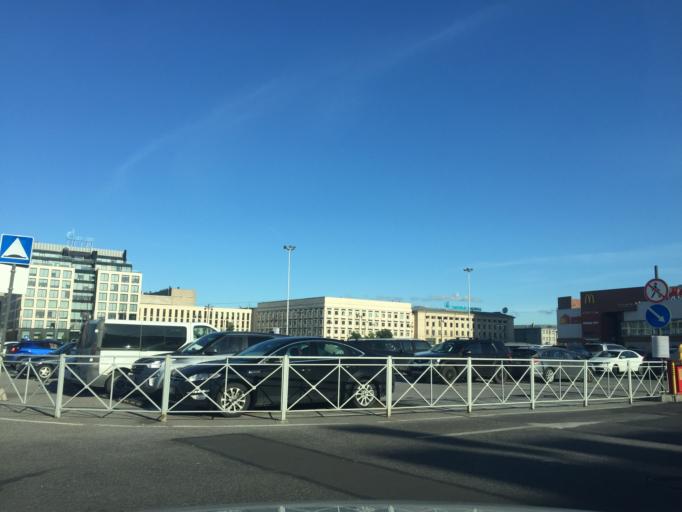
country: RU
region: St.-Petersburg
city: Admiralteisky
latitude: 59.8823
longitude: 30.3165
